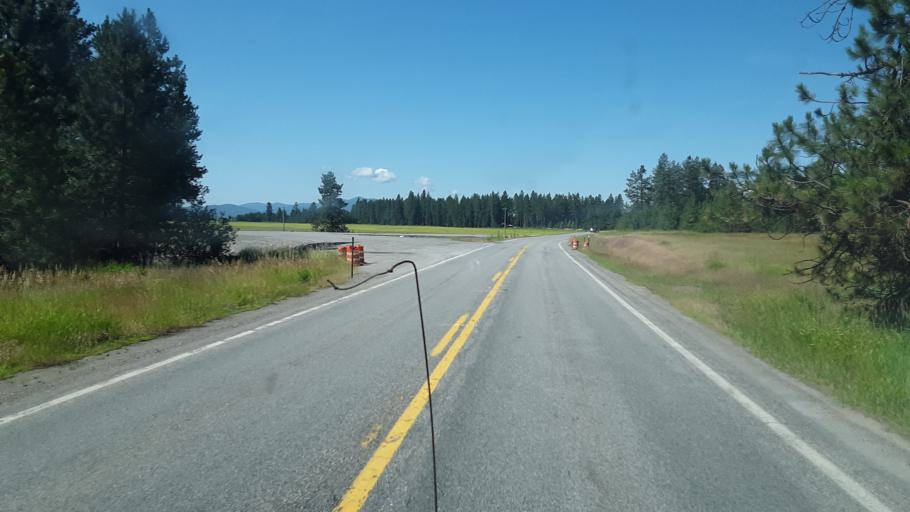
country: US
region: Idaho
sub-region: Kootenai County
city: Hayden
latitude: 47.8191
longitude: -116.7958
